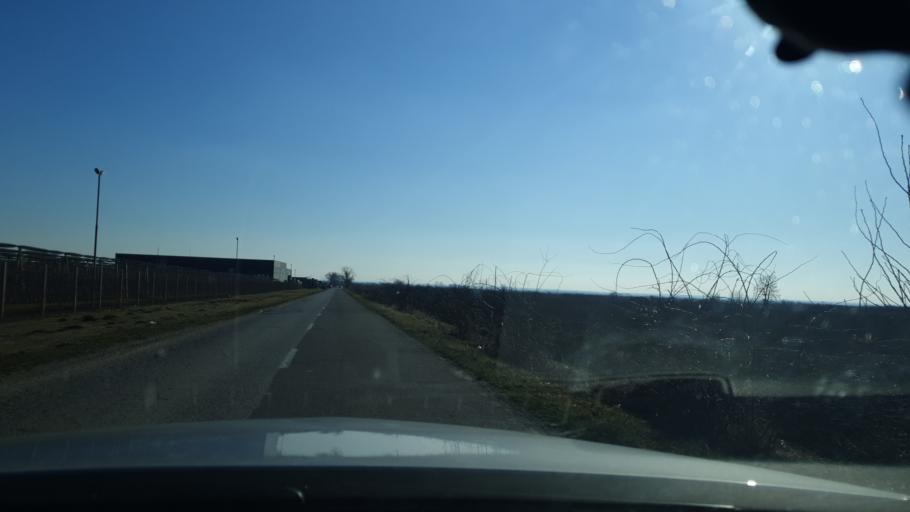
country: RS
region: Autonomna Pokrajina Vojvodina
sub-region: Sremski Okrug
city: Ruma
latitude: 45.0544
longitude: 19.8071
